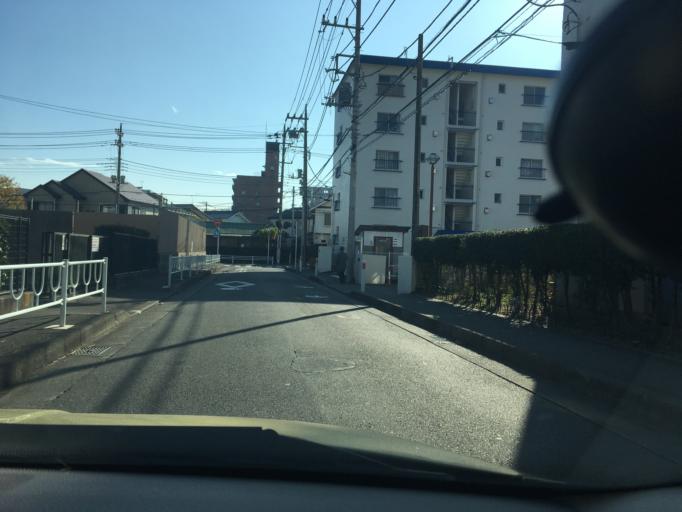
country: JP
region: Tokyo
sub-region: Machida-shi
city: Machida
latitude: 35.5736
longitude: 139.3953
